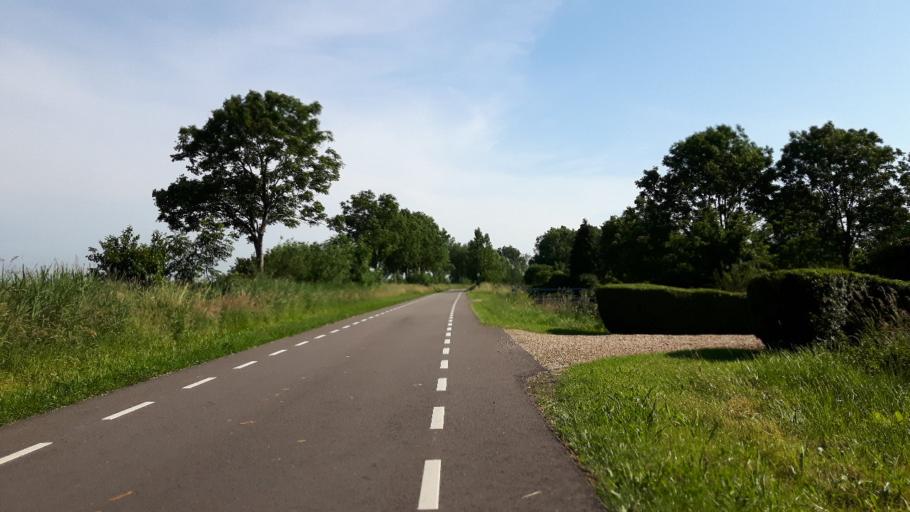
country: NL
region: Utrecht
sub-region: Stichtse Vecht
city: Breukelen
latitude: 52.1893
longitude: 4.9590
